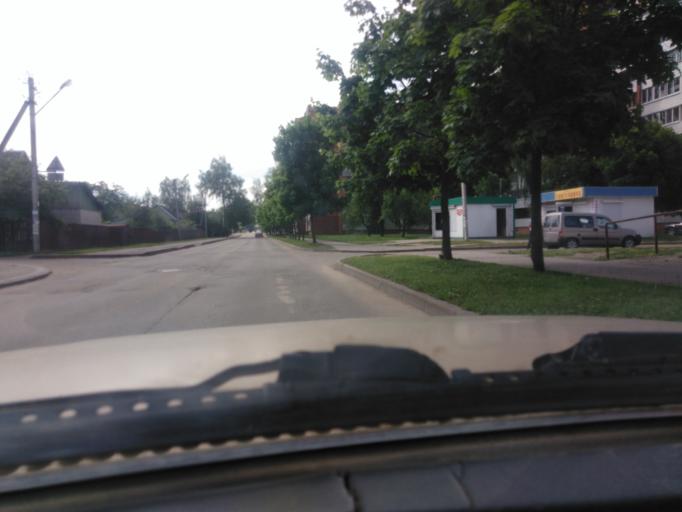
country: BY
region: Mogilev
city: Mahilyow
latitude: 53.9325
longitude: 30.3578
